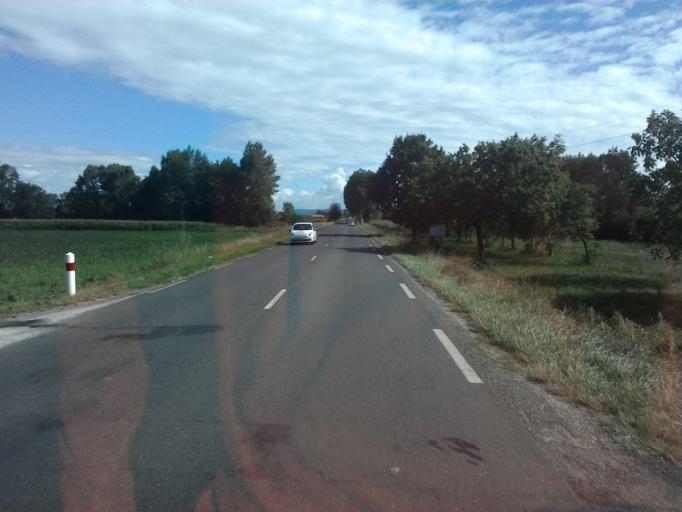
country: FR
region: Rhone-Alpes
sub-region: Departement de l'Ain
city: Ambronay
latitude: 45.9861
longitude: 5.3494
